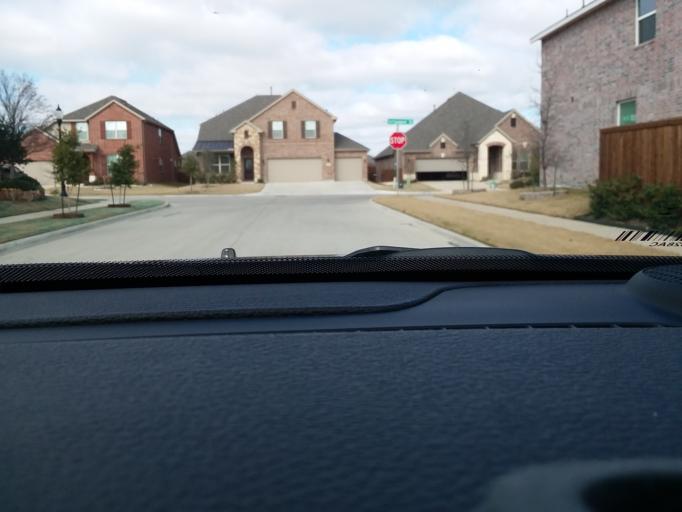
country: US
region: Texas
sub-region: Denton County
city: Little Elm
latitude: 33.2412
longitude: -96.8980
